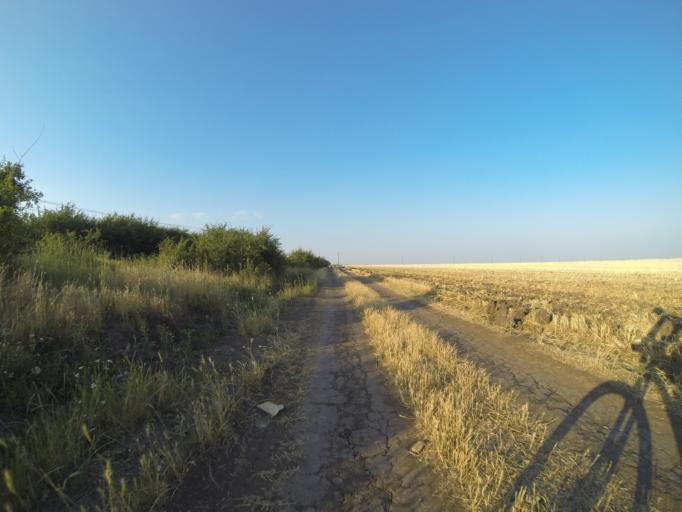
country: RO
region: Dolj
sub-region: Comuna Ceratu
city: Ceratu
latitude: 44.0474
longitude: 23.6632
